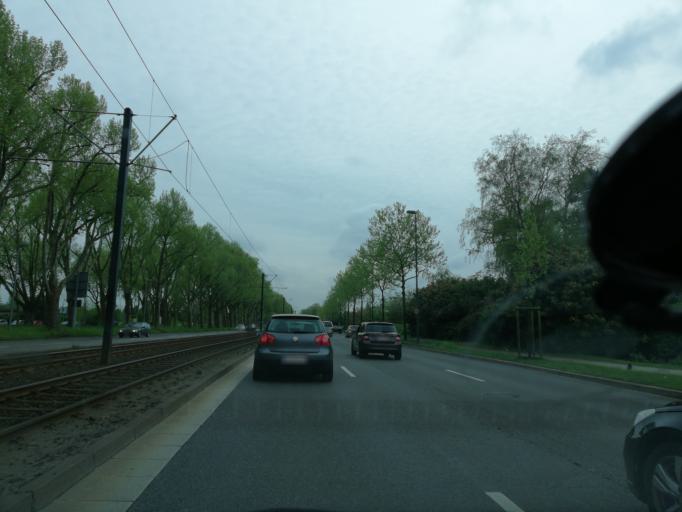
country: DE
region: North Rhine-Westphalia
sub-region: Regierungsbezirk Dusseldorf
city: Dusseldorf
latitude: 51.2057
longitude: 6.7566
